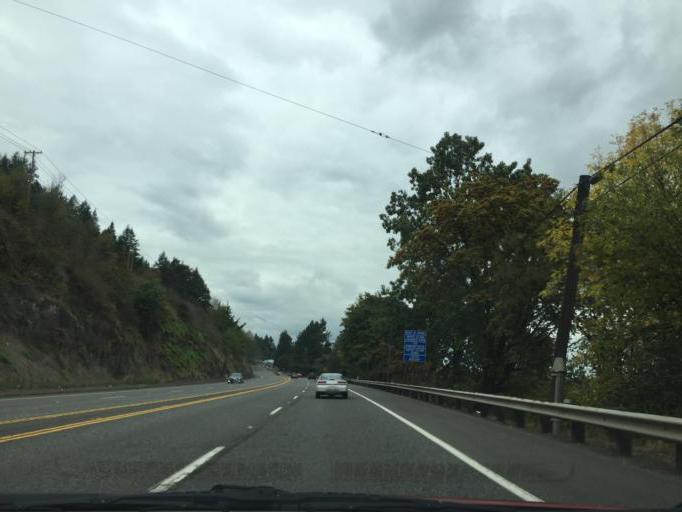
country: US
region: Oregon
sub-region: Washington County
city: Bethany
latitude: 45.6218
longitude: -122.8121
